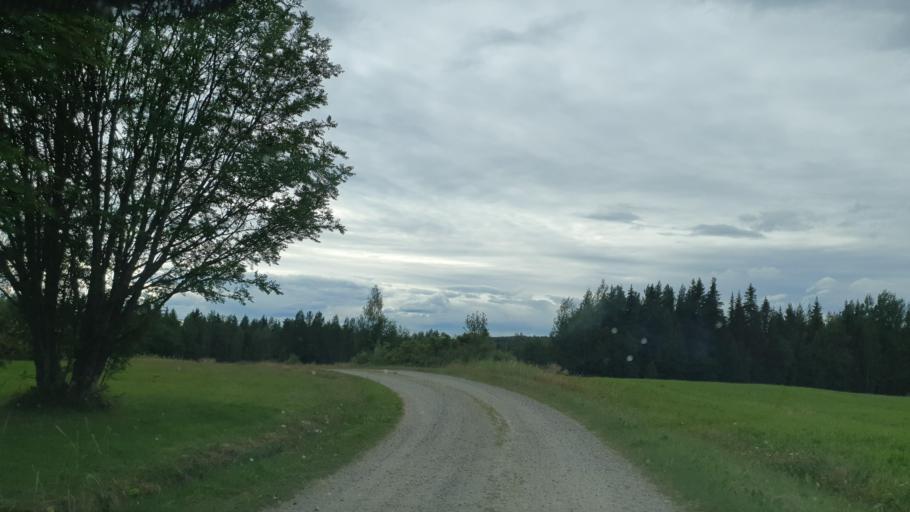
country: FI
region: Kainuu
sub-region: Kehys-Kainuu
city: Kuhmo
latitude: 64.2034
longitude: 29.3787
